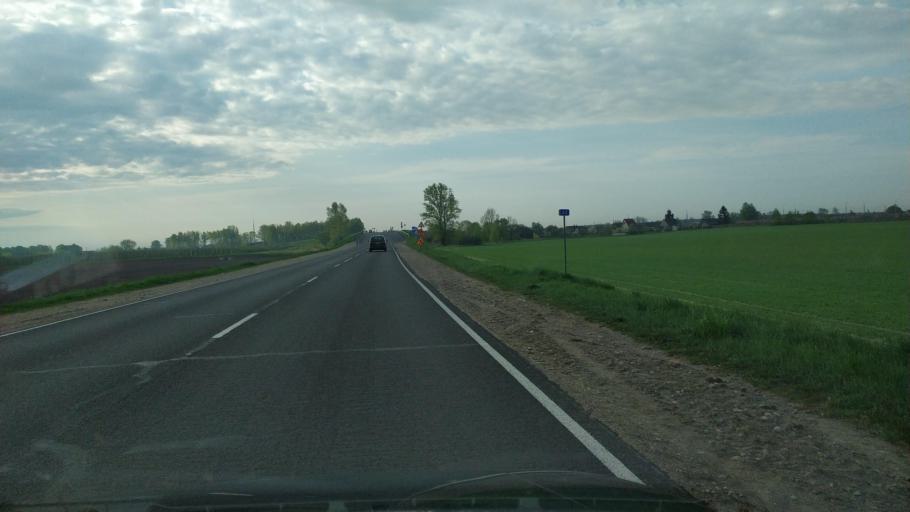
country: BY
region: Brest
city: Zhabinka
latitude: 52.1598
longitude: 24.0503
